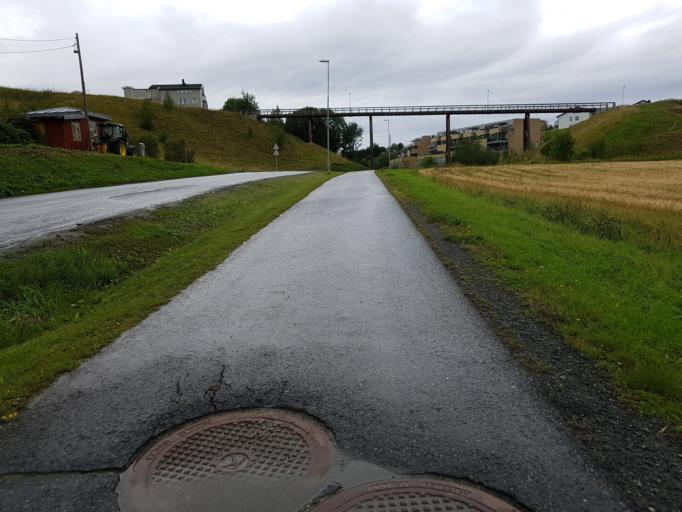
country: NO
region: Sor-Trondelag
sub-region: Trondheim
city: Trondheim
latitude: 63.3840
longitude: 10.4311
